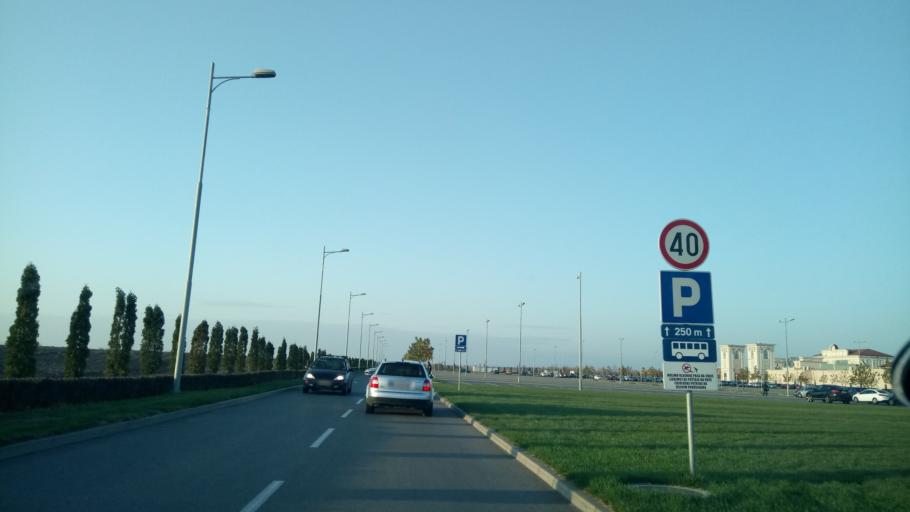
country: RS
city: Novi Karlovci
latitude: 45.0674
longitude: 20.1357
